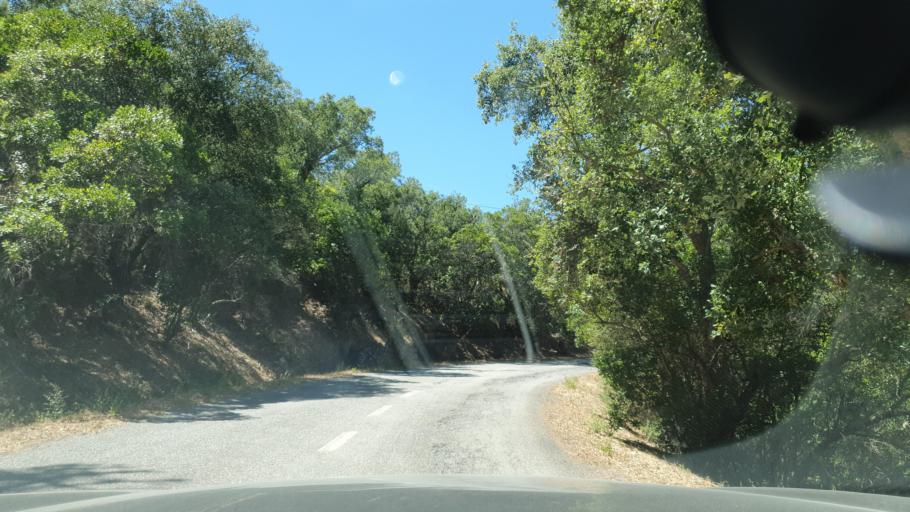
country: PT
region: Beja
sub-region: Odemira
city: Odemira
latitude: 37.6090
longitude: -8.5001
